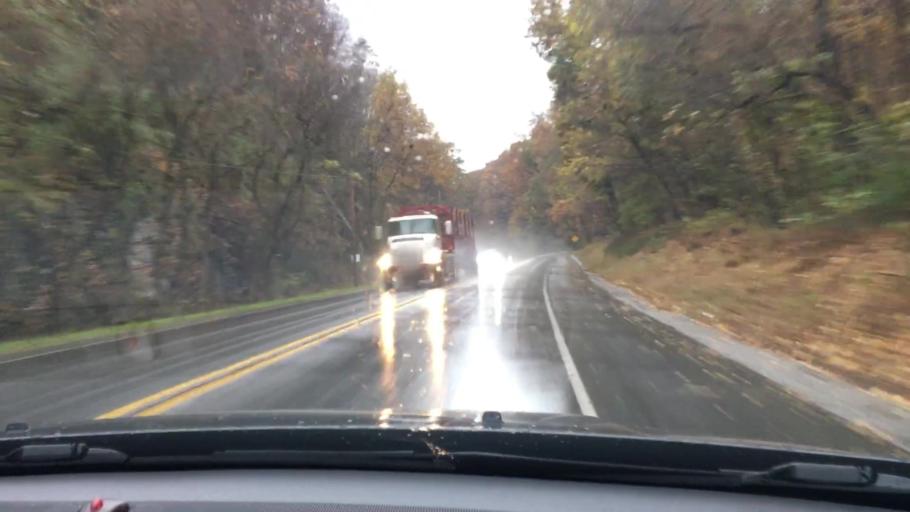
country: US
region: Pennsylvania
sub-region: York County
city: Susquehanna Trails
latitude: 39.8105
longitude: -76.3313
